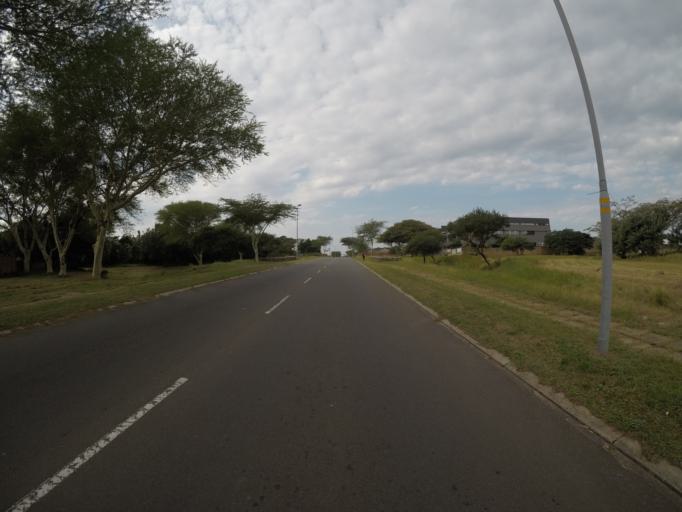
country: ZA
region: KwaZulu-Natal
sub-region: uThungulu District Municipality
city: Richards Bay
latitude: -28.7379
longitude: 32.0808
